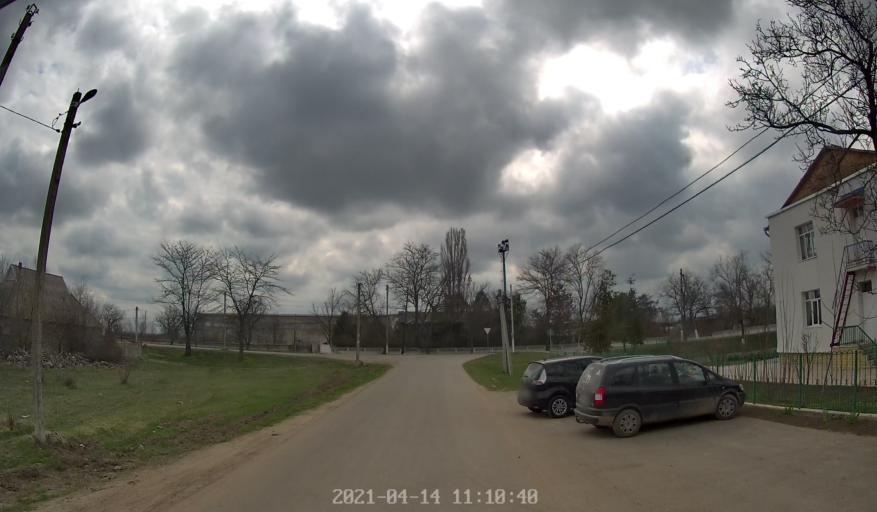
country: MD
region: Criuleni
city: Criuleni
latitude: 47.1555
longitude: 29.1485
